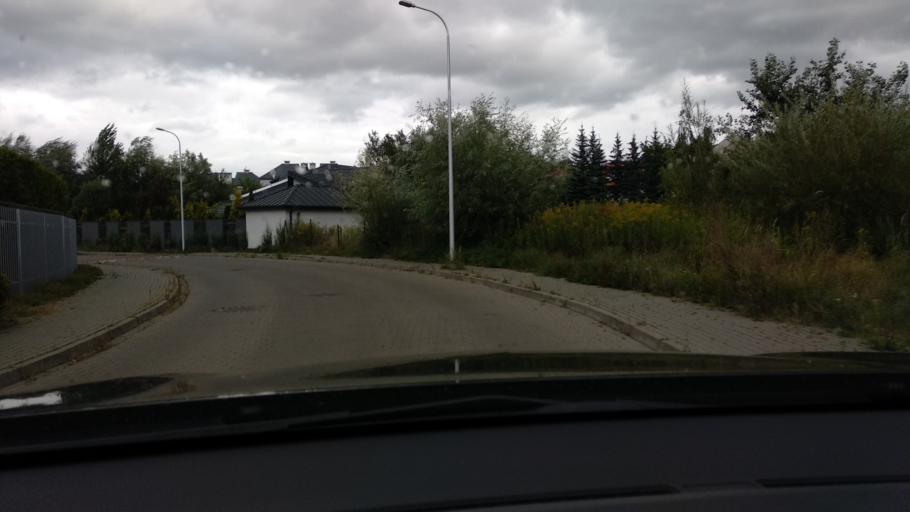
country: PL
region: Masovian Voivodeship
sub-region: Warszawa
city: Ursynow
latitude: 52.1297
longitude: 21.0520
